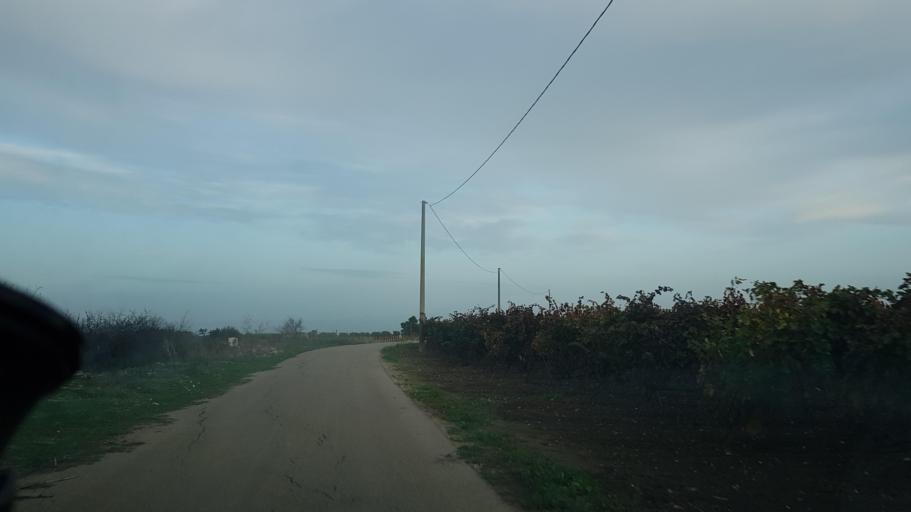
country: IT
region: Apulia
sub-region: Provincia di Brindisi
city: San Pancrazio Salentino
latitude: 40.4213
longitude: 17.8557
